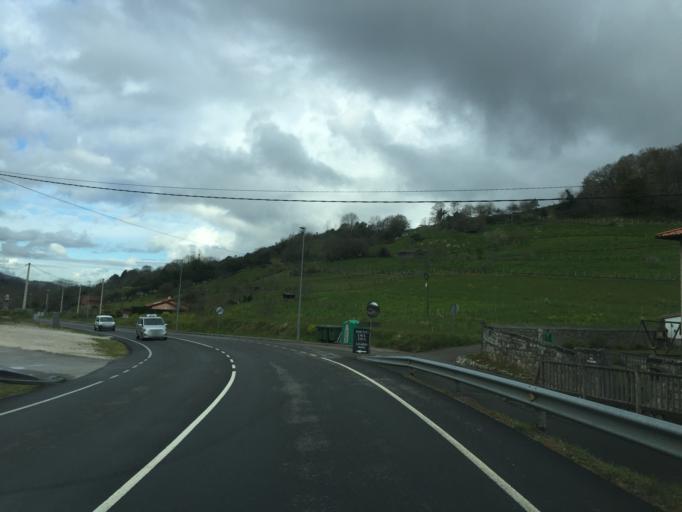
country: ES
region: Asturias
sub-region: Province of Asturias
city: Carrena
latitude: 43.3350
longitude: -4.9542
